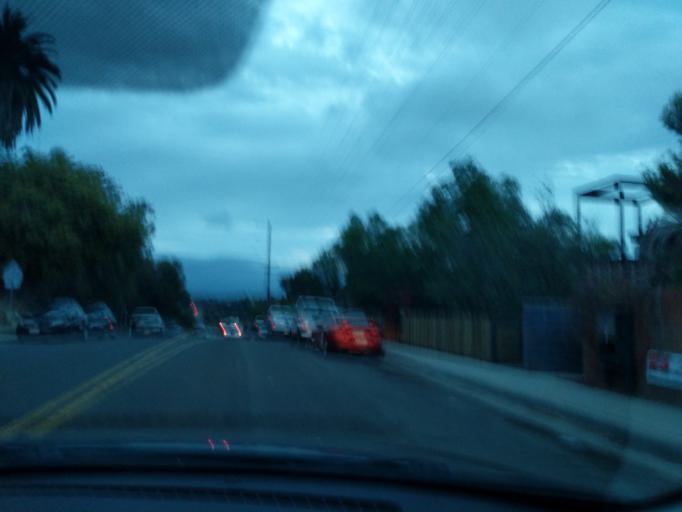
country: US
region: California
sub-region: San Diego County
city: San Diego
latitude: 32.7170
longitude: -117.1221
